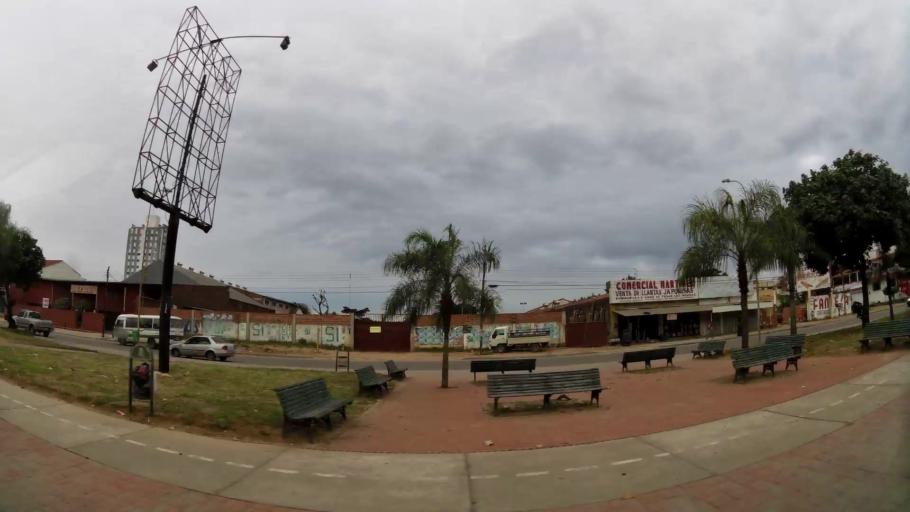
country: BO
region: Santa Cruz
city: Santa Cruz de la Sierra
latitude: -17.8247
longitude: -63.1847
